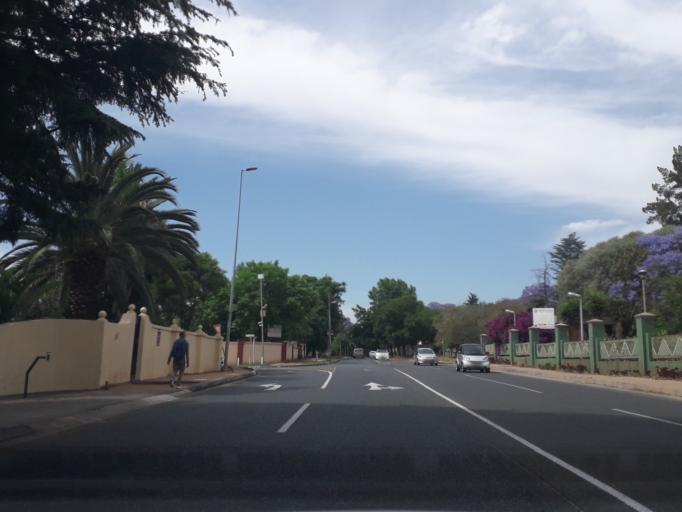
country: ZA
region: Gauteng
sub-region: City of Johannesburg Metropolitan Municipality
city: Johannesburg
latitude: -26.0765
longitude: 27.9961
